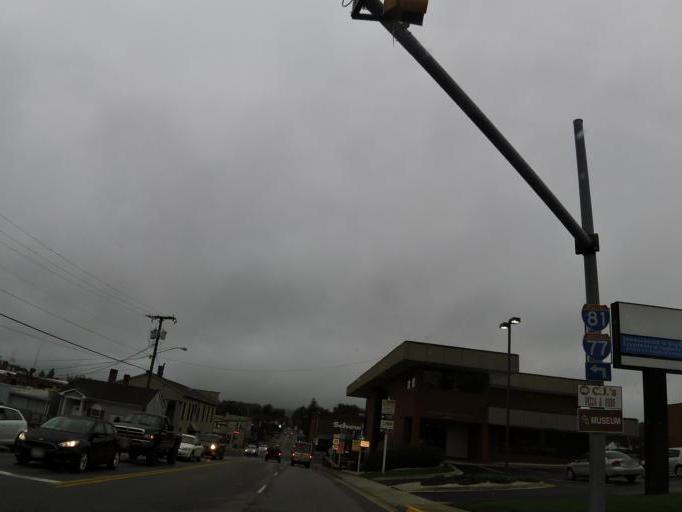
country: US
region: Virginia
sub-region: Wythe County
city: Wytheville
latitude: 36.9492
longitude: -81.0860
